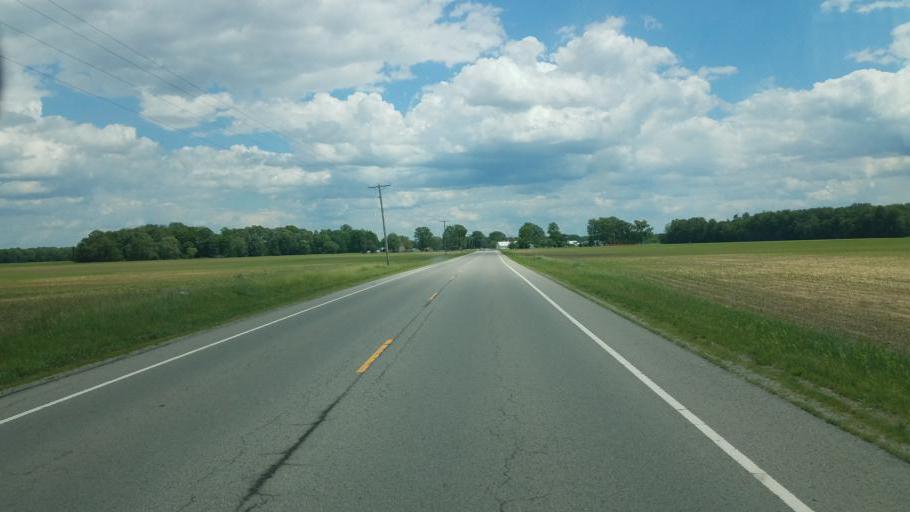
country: US
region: Ohio
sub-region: Crawford County
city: Galion
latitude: 40.8099
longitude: -82.8293
